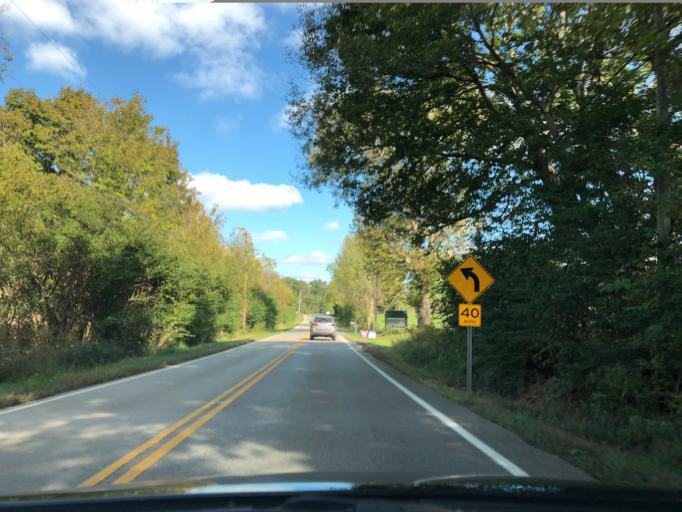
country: US
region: Ohio
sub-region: Warren County
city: Loveland Park
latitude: 39.2867
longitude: -84.2142
